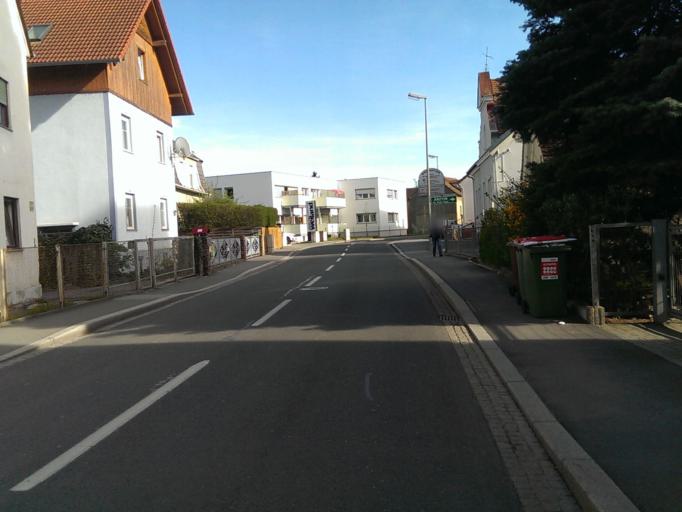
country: AT
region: Styria
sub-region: Graz Stadt
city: Graz
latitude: 47.0462
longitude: 15.4526
